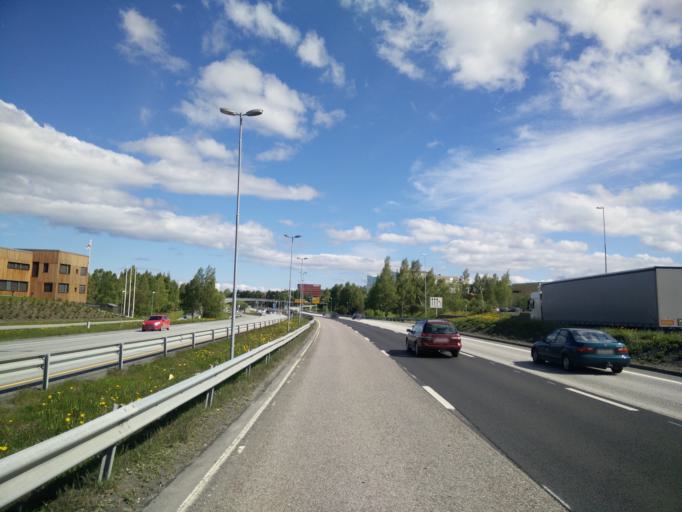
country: NO
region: Sor-Trondelag
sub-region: Trondheim
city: Trondheim
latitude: 63.3958
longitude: 10.3910
